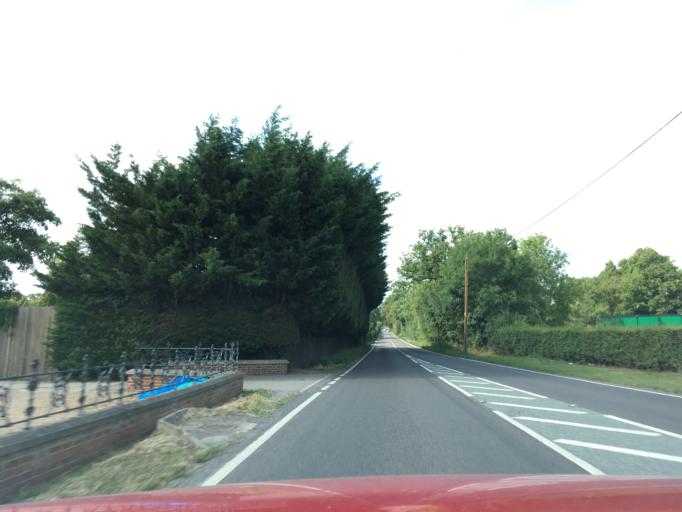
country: GB
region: England
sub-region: Kent
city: Headcorn
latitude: 51.1884
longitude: 0.6055
